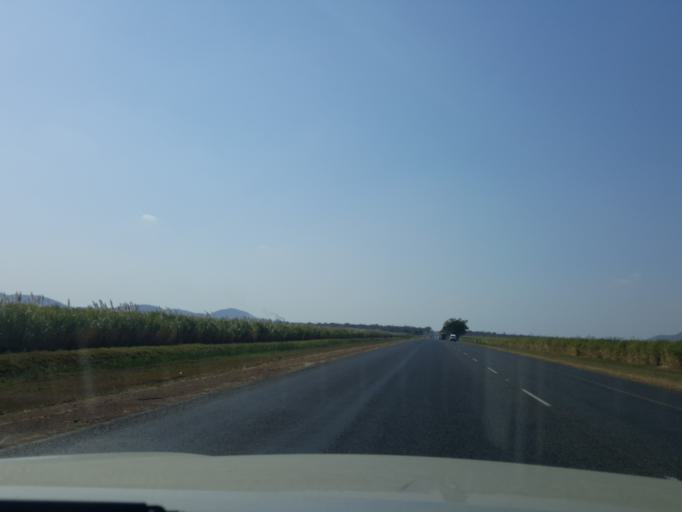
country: SZ
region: Hhohho
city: Ntfonjeni
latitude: -25.4884
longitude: 31.5332
